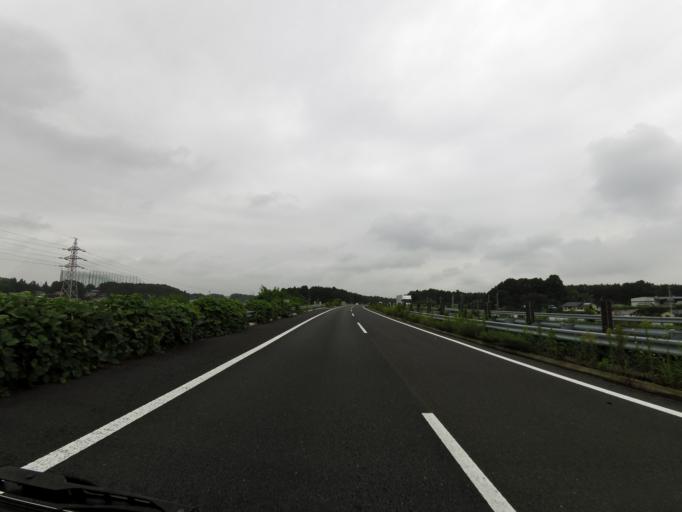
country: JP
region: Tochigi
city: Mooka
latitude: 36.4229
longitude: 139.9815
